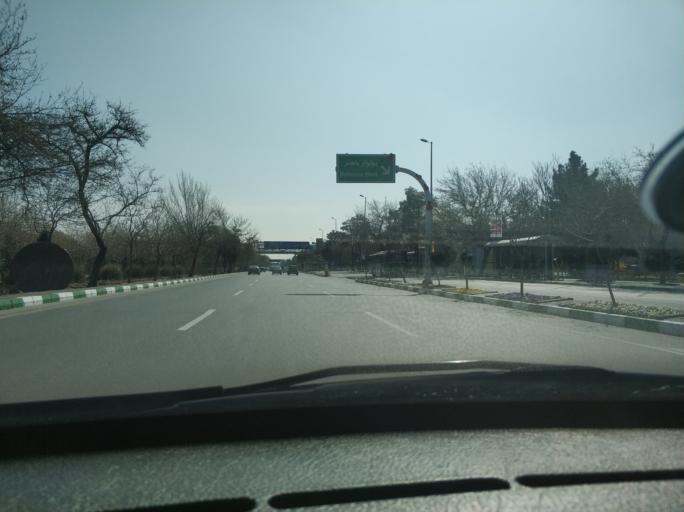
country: IR
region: Razavi Khorasan
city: Mashhad
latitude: 36.3194
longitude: 59.5263
